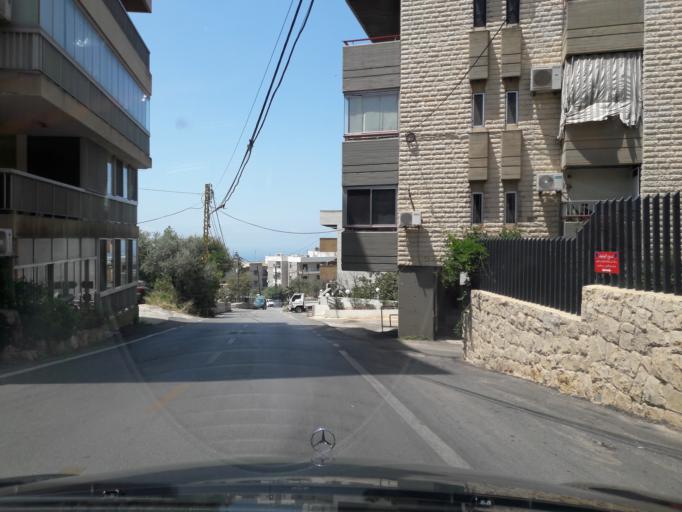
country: LB
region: Mont-Liban
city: Djounie
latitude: 33.9338
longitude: 35.6224
